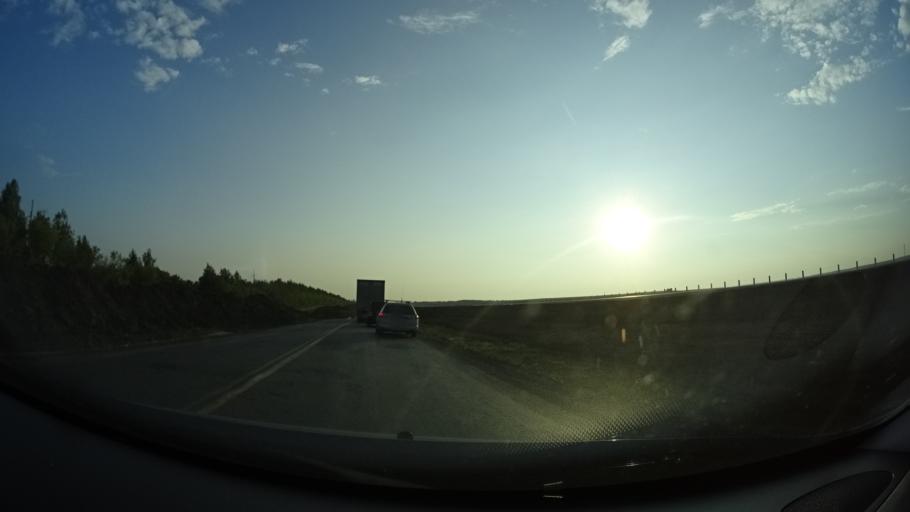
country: RU
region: Samara
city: Kamyshla
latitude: 54.0369
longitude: 51.9525
